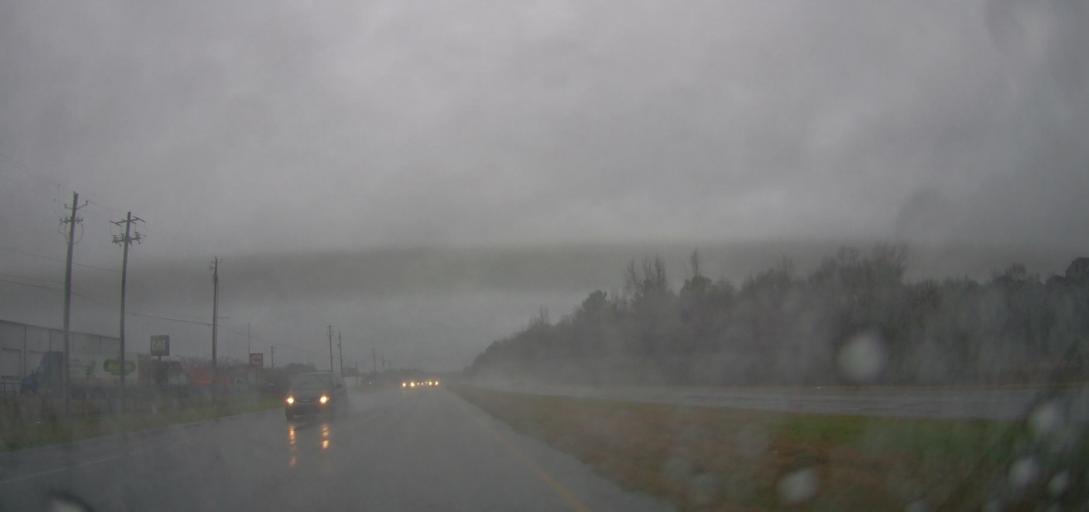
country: US
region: Alabama
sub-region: Montgomery County
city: Montgomery
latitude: 32.3807
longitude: -86.3788
